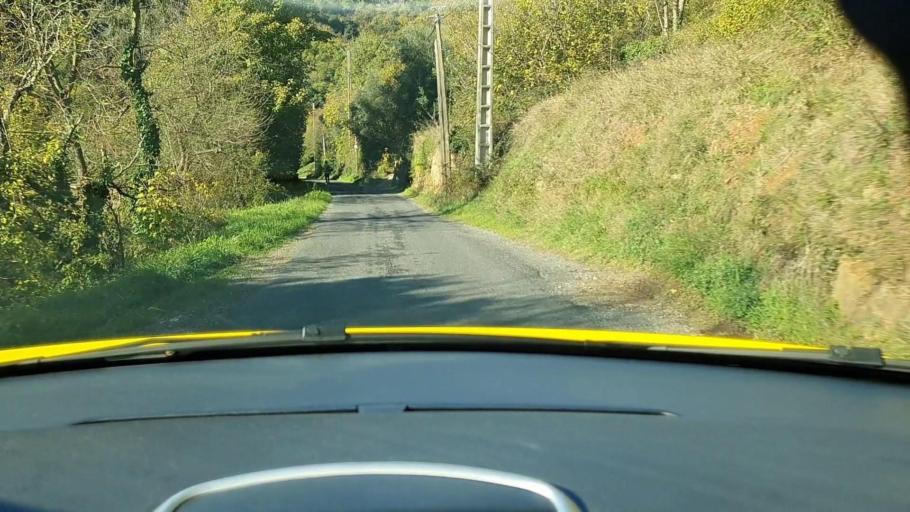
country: FR
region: Languedoc-Roussillon
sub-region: Departement du Gard
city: Le Vigan
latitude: 43.9962
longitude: 3.6221
